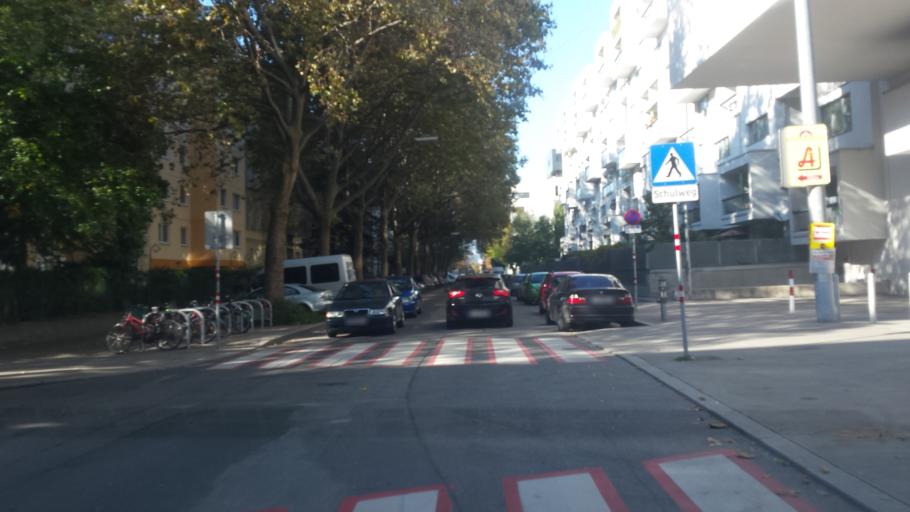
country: AT
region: Vienna
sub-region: Wien Stadt
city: Vienna
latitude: 48.2192
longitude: 16.4083
